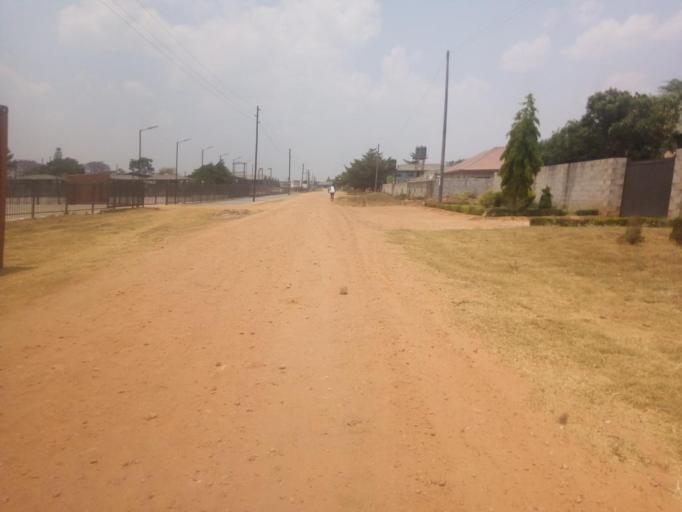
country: ZM
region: Lusaka
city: Lusaka
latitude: -15.3946
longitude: 28.3939
